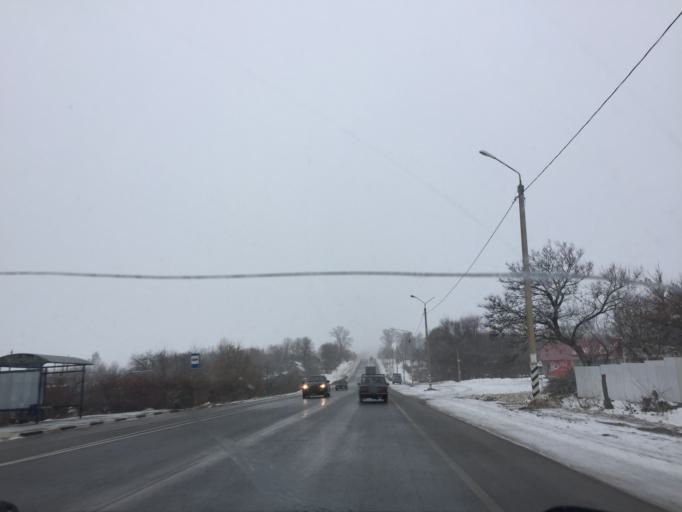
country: RU
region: Tula
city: Plavsk
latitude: 53.8138
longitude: 37.3935
